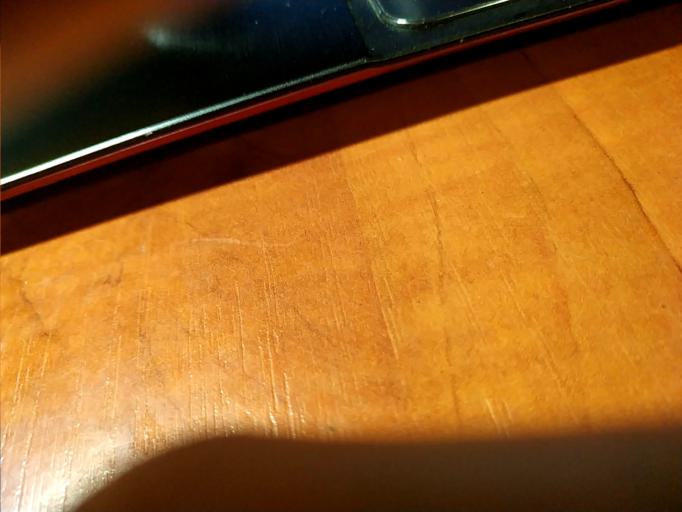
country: RU
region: Tverskaya
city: Ves'yegonsk
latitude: 58.7199
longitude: 37.5439
